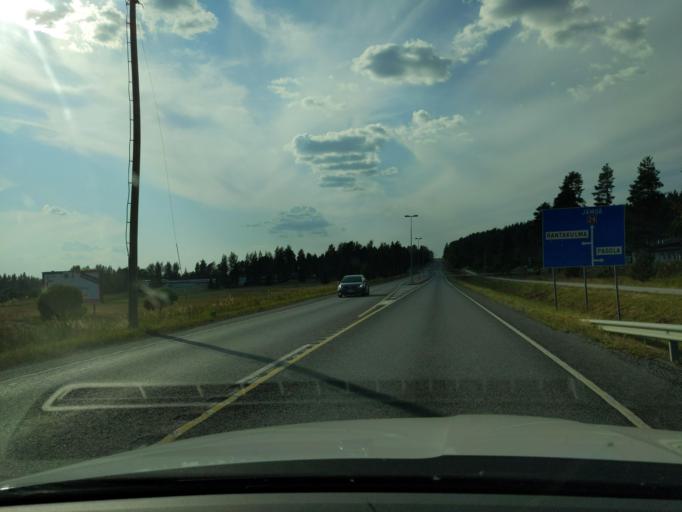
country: FI
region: Paijanne Tavastia
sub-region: Lahti
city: Asikkala
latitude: 61.1604
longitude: 25.5815
